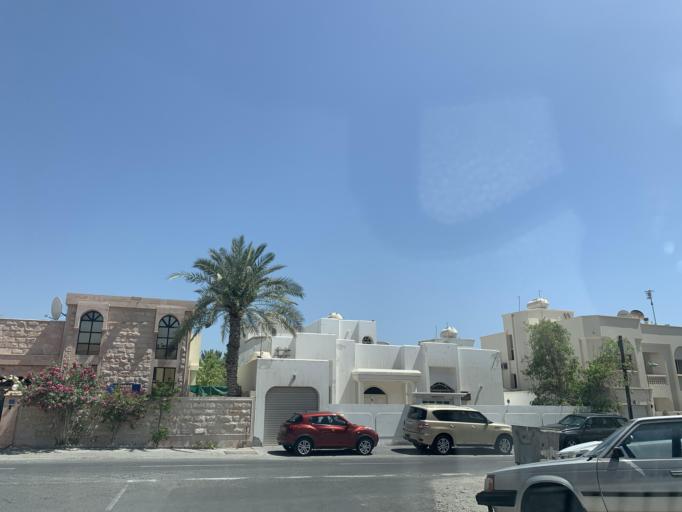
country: BH
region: Northern
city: Ar Rifa'
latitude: 26.1334
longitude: 50.5796
